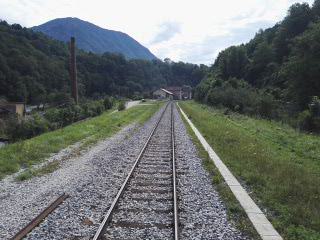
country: SI
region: Tolmin
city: Tolmin
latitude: 46.1596
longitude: 13.8111
